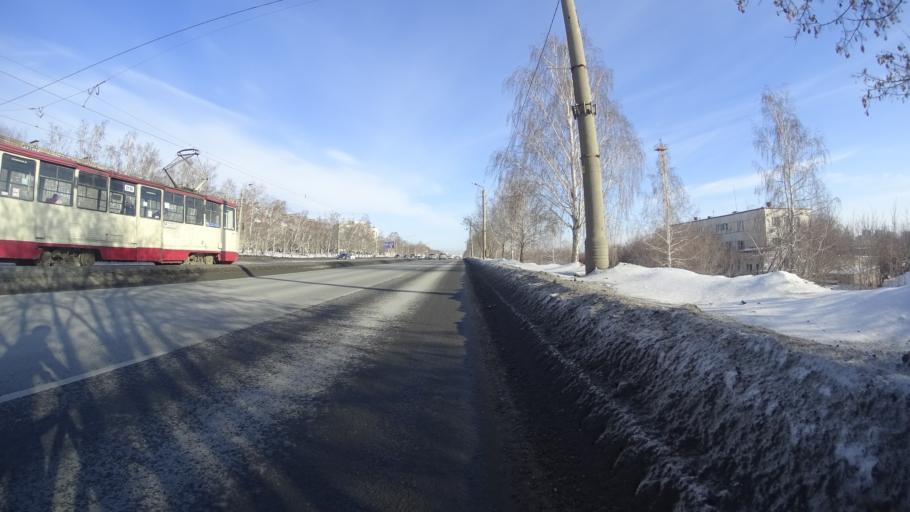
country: RU
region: Chelyabinsk
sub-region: Gorod Chelyabinsk
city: Chelyabinsk
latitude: 55.1889
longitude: 61.3421
